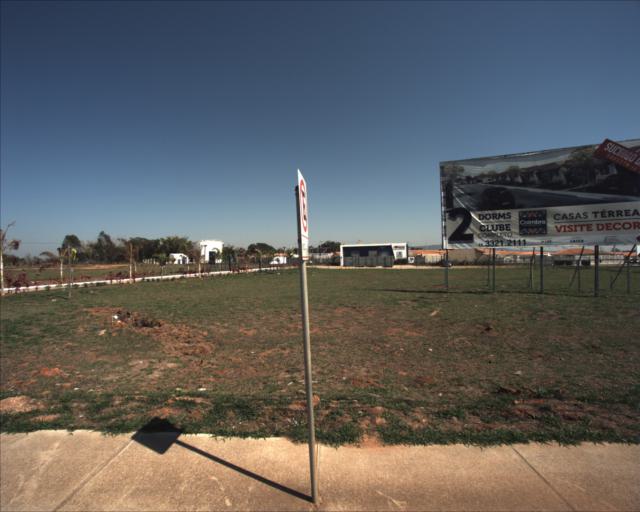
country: BR
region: Sao Paulo
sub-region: Sorocaba
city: Sorocaba
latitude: -23.4937
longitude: -47.5317
